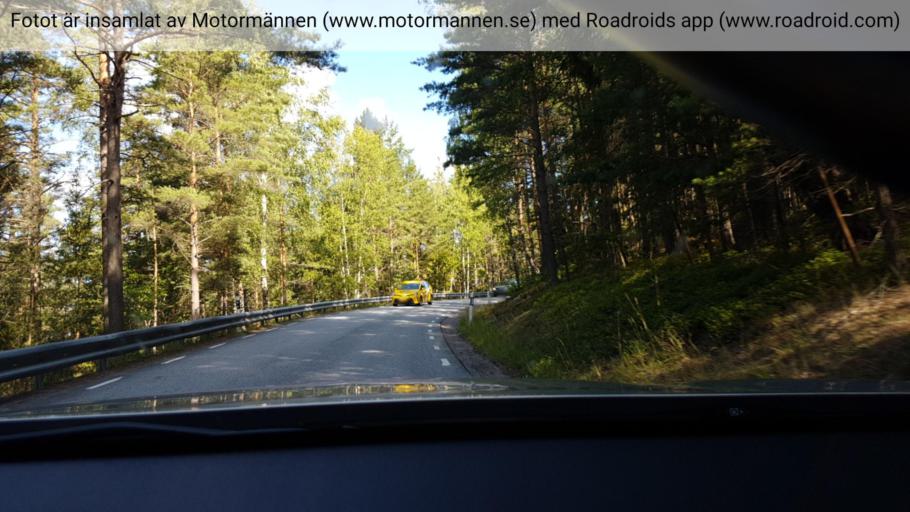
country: SE
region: Stockholm
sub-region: Norrtalje Kommun
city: Norrtalje
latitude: 59.6789
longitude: 18.8357
